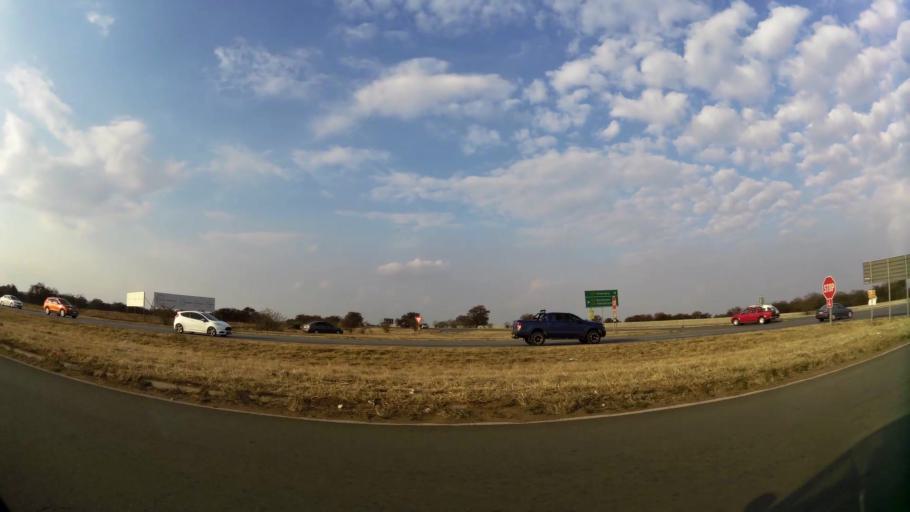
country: ZA
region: Gauteng
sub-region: Sedibeng District Municipality
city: Vereeniging
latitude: -26.6346
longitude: 27.8697
